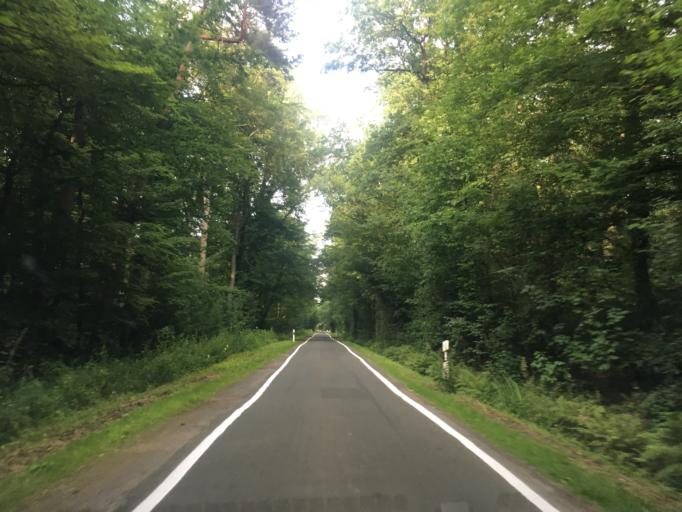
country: DE
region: North Rhine-Westphalia
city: Ludinghausen
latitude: 51.7959
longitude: 7.4221
